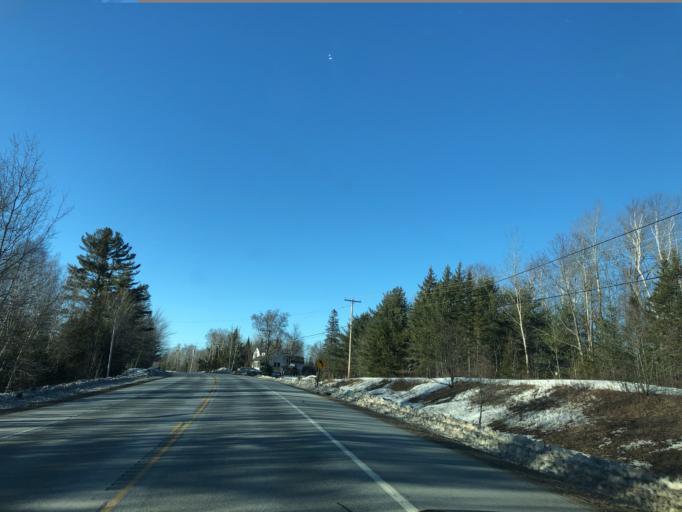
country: US
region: Maine
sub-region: Penobscot County
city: Kenduskeag
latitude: 44.9463
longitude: -68.9454
